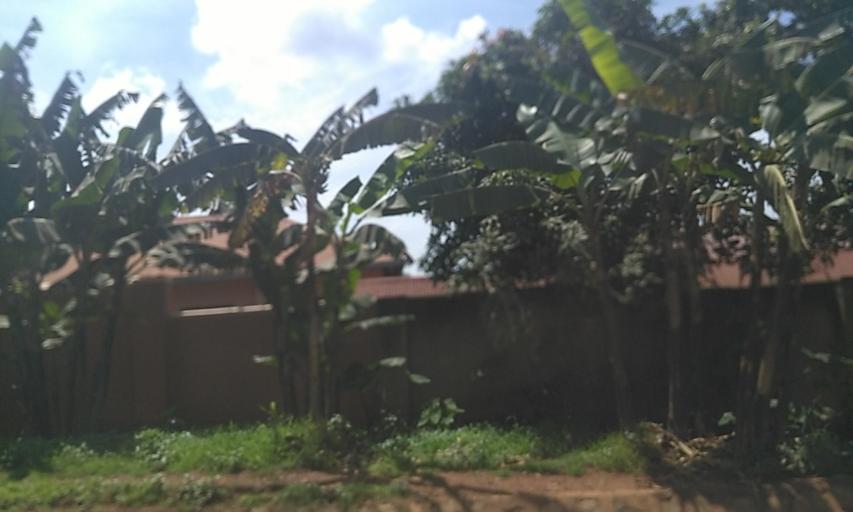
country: UG
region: Central Region
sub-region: Wakiso District
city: Wakiso
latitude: 0.3922
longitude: 32.5039
